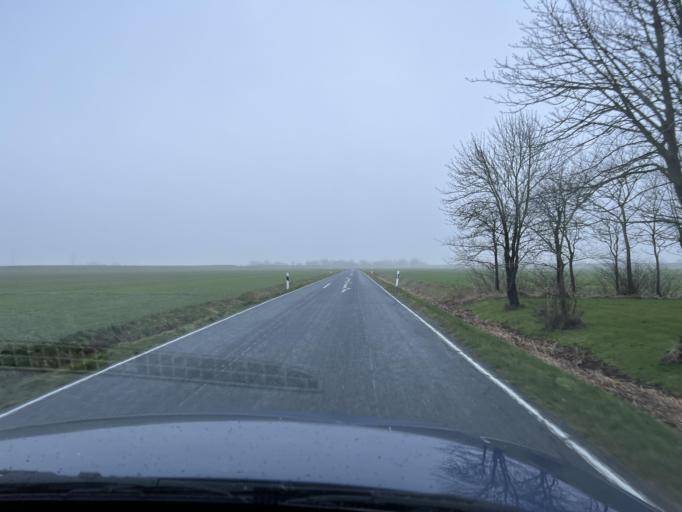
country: DE
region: Schleswig-Holstein
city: Strubbel
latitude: 54.2709
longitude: 8.9447
